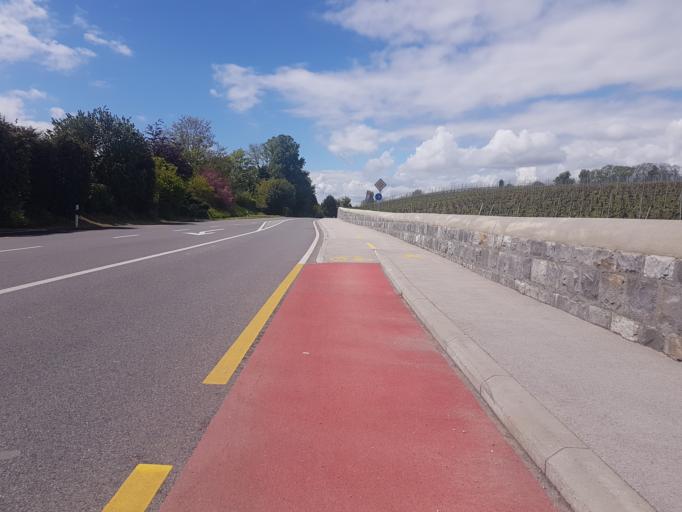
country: CH
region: Vaud
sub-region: Nyon District
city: Gland
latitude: 46.4298
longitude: 6.3006
